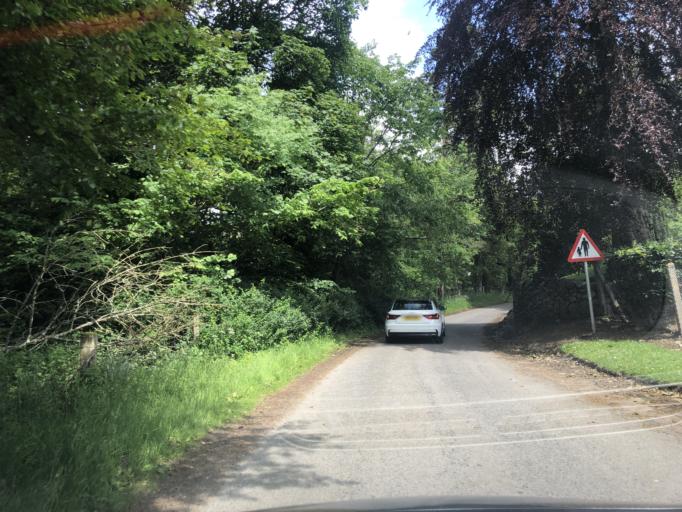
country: GB
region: Scotland
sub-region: Angus
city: Kirriemuir
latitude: 56.8433
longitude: -3.1056
